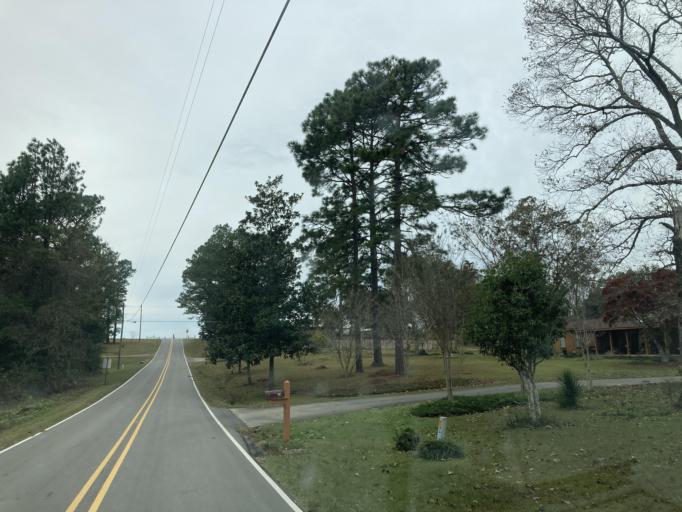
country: US
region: Mississippi
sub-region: Lamar County
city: Purvis
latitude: 31.1104
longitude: -89.4164
